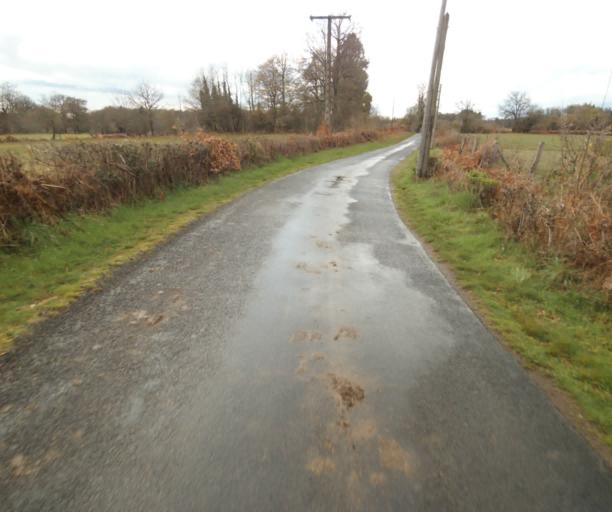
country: FR
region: Limousin
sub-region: Departement de la Correze
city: Saint-Privat
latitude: 45.2201
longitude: 2.0185
